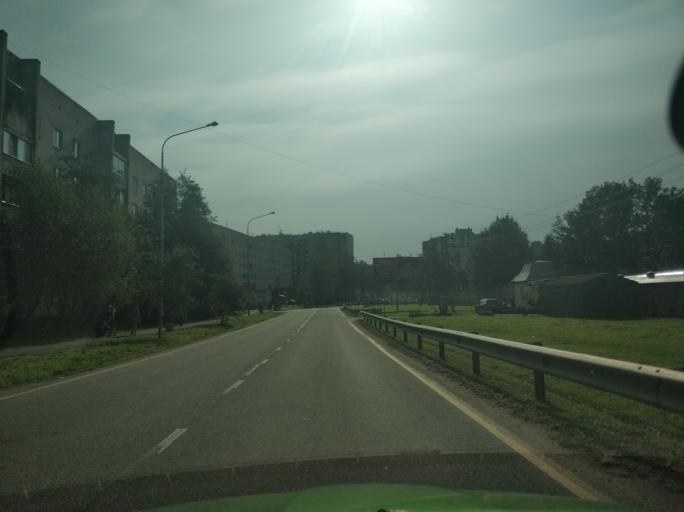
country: RU
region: Leningrad
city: Murino
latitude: 60.0461
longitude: 30.4619
